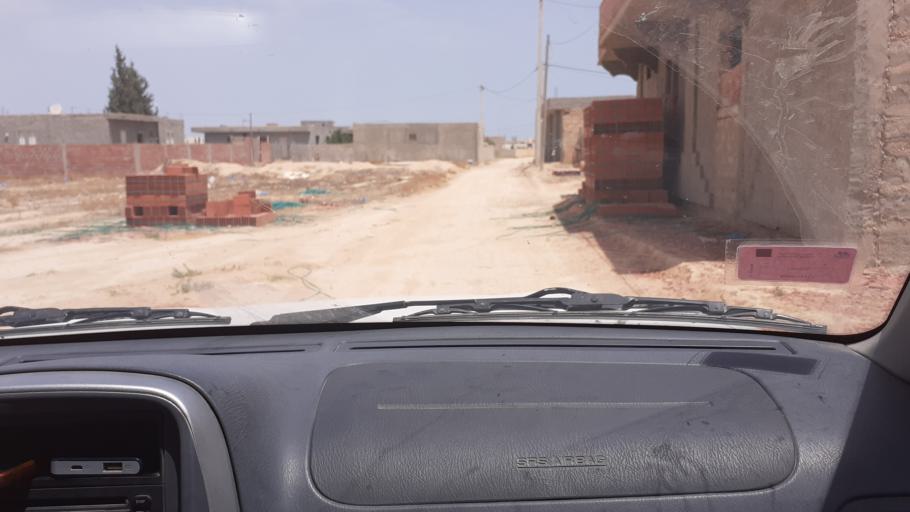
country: TN
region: Qabis
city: Matmata
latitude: 33.6086
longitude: 10.2892
